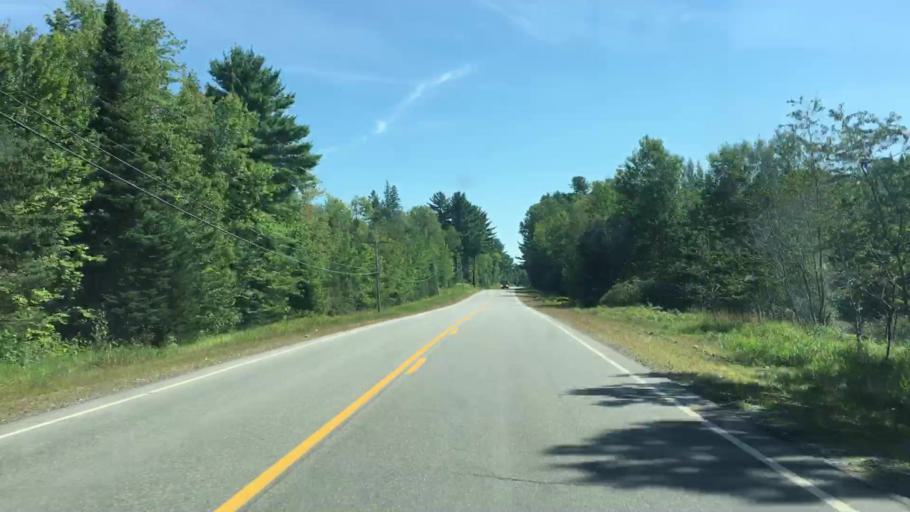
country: US
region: Maine
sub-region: Piscataquis County
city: Milo
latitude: 45.1941
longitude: -68.9012
